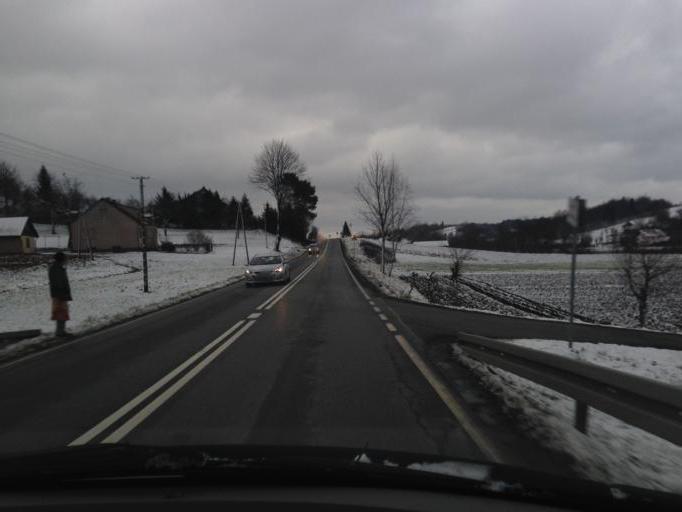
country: PL
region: Lesser Poland Voivodeship
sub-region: Powiat tarnowski
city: Siemiechow
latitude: 49.8550
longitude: 20.8866
